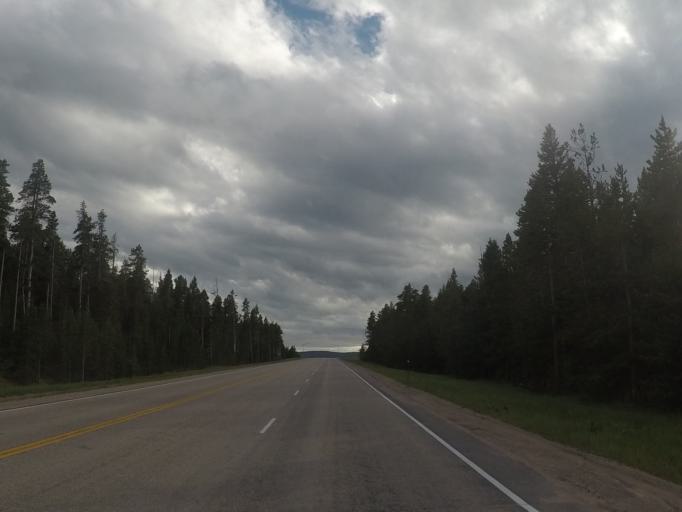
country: US
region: Wyoming
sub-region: Sheridan County
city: Sheridan
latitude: 44.7886
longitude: -107.4921
